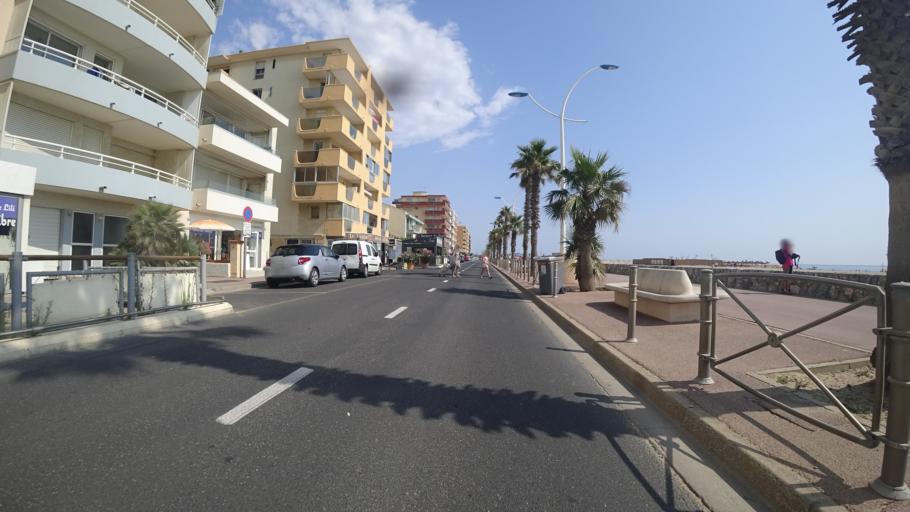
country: FR
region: Languedoc-Roussillon
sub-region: Departement des Pyrenees-Orientales
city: Canet-en-Roussillon
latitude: 42.6979
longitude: 3.0362
